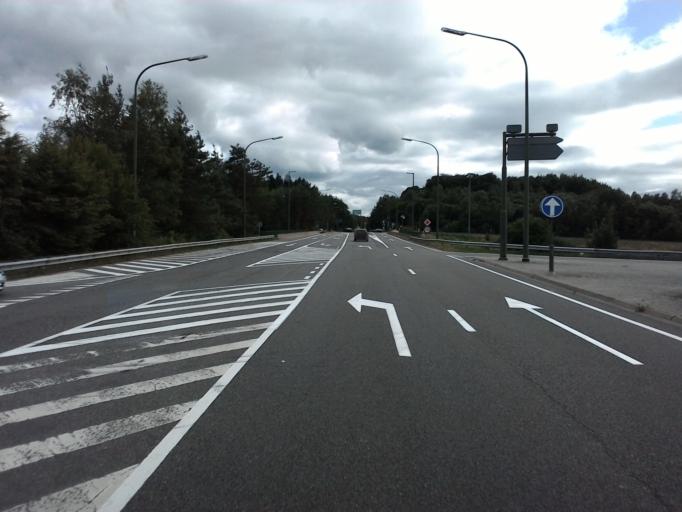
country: BE
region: Wallonia
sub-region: Province du Luxembourg
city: Arlon
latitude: 49.6726
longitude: 5.7780
